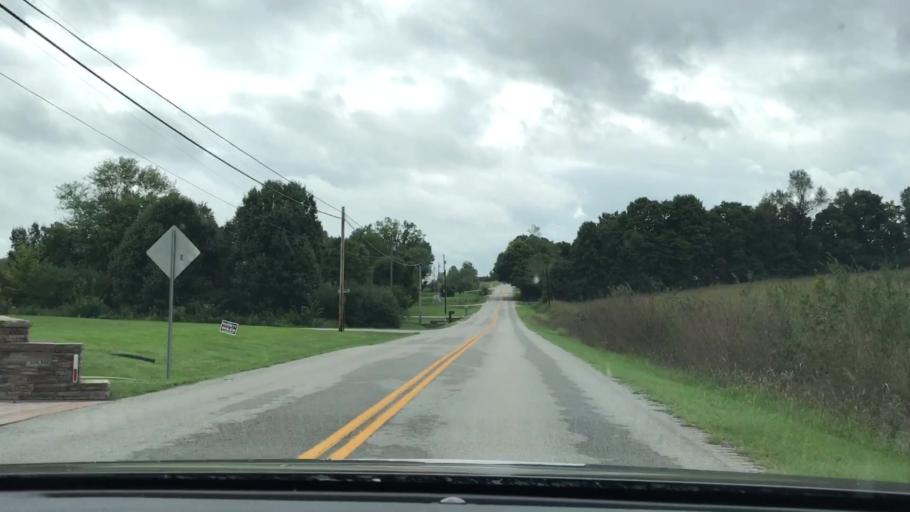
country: US
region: Kentucky
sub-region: Barren County
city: Glasgow
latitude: 36.9610
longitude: -85.8654
